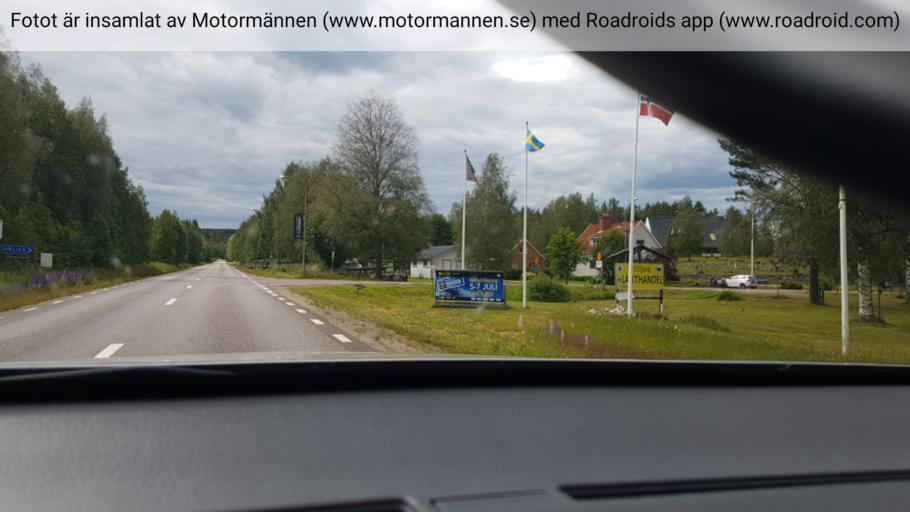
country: NO
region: Hedmark
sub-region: Trysil
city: Innbygda
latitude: 60.8983
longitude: 12.5937
